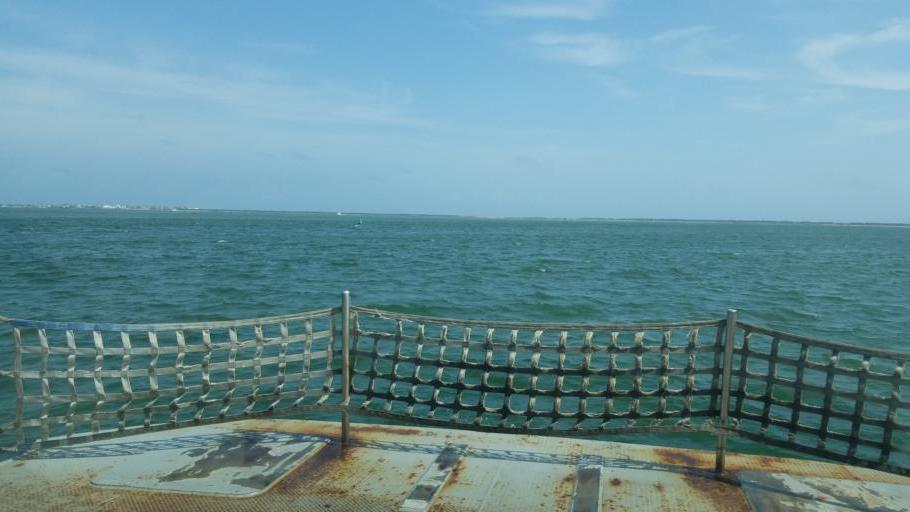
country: US
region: North Carolina
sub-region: Dare County
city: Buxton
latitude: 35.2168
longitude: -75.7364
